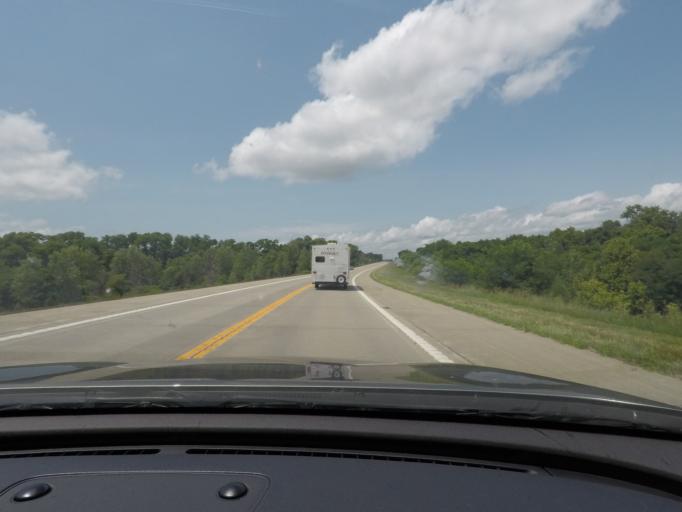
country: US
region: Missouri
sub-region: Carroll County
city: Carrollton
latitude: 39.2015
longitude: -93.4981
